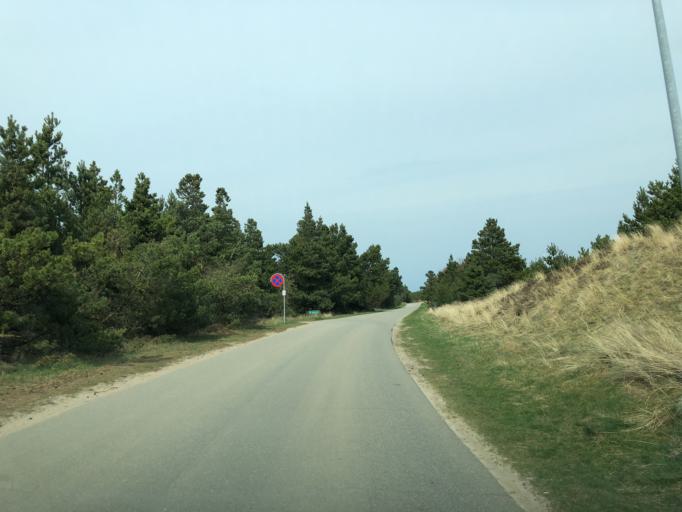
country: DK
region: South Denmark
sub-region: Varde Kommune
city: Oksbol
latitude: 55.5593
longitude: 8.1337
